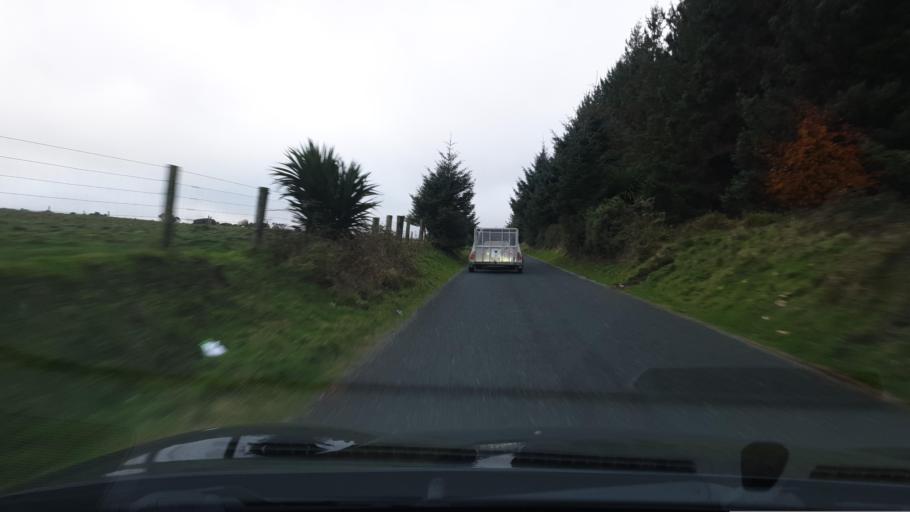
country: IE
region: Leinster
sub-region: Wicklow
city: Enniskerry
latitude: 53.1497
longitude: -6.1886
